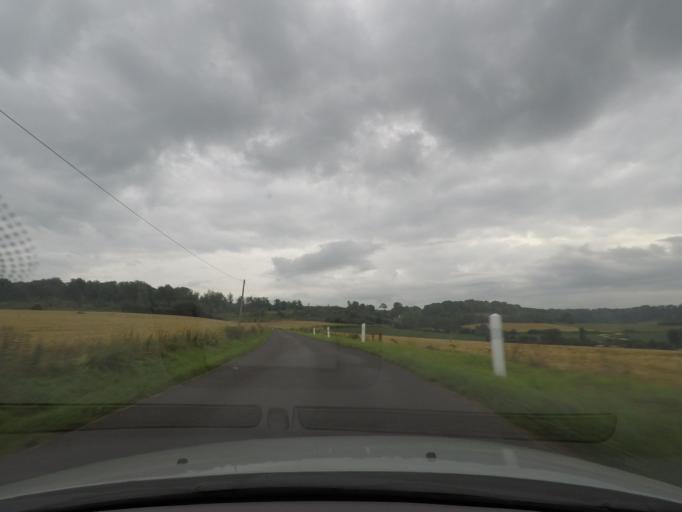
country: FR
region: Haute-Normandie
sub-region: Departement de la Seine-Maritime
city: Neufchatel-en-Bray
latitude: 49.7295
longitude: 1.4653
